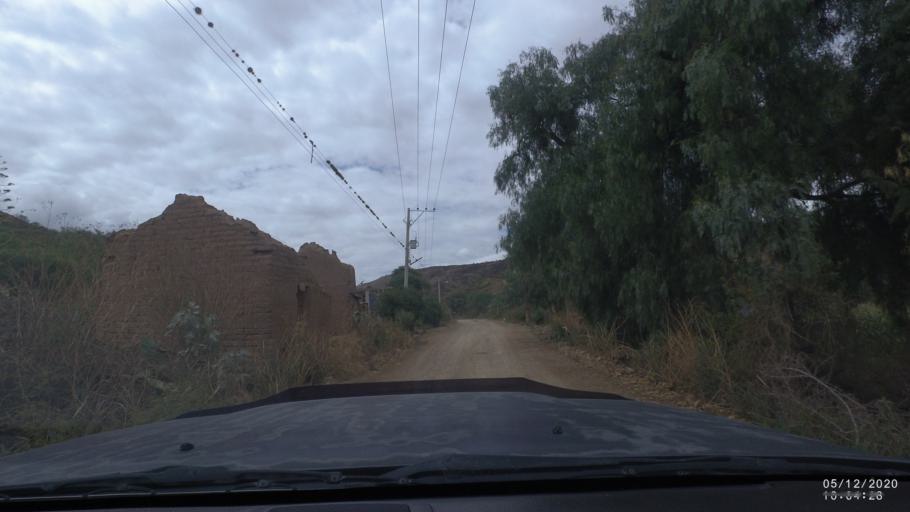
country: BO
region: Cochabamba
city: Sipe Sipe
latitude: -17.4633
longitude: -66.2861
